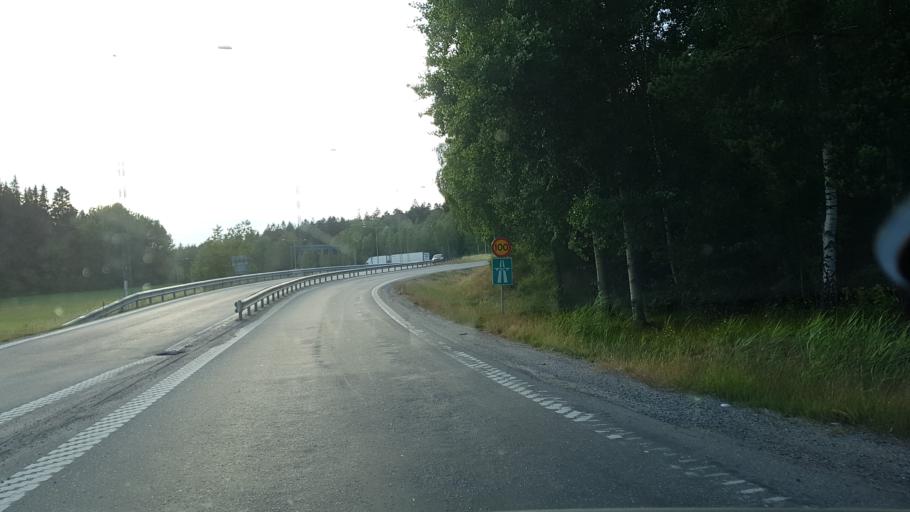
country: SE
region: Stockholm
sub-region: Salems Kommun
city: Ronninge
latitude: 59.2111
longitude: 17.7541
